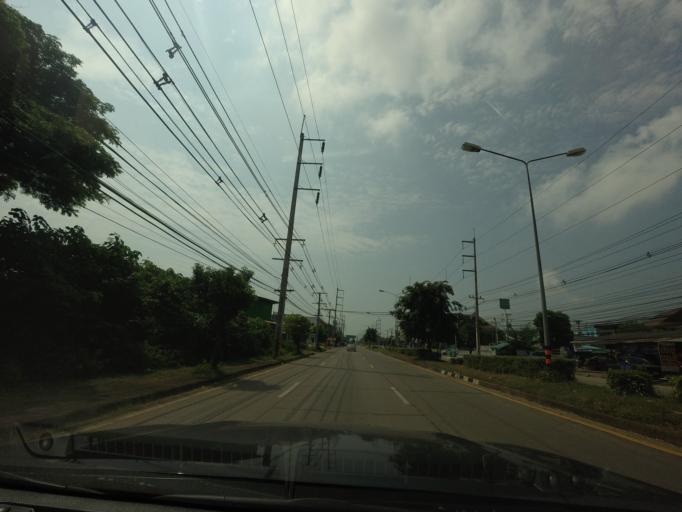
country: TH
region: Phrae
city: Phrae
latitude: 18.1146
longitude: 100.1385
